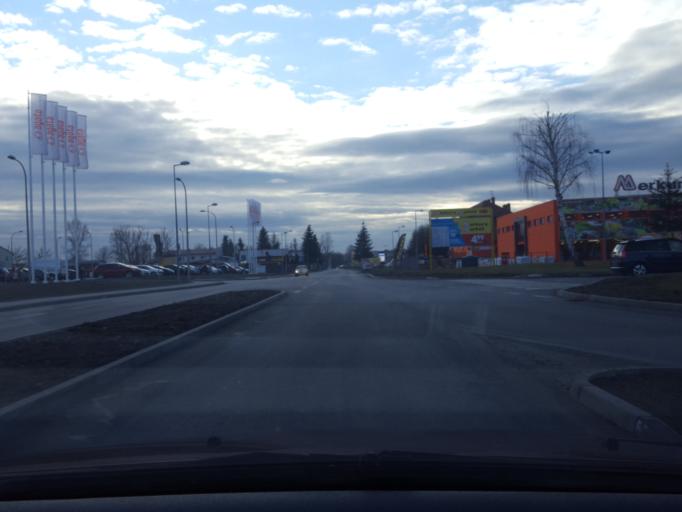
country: PL
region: Lesser Poland Voivodeship
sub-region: Powiat nowosadecki
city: Nawojowa
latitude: 49.6022
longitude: 20.7289
